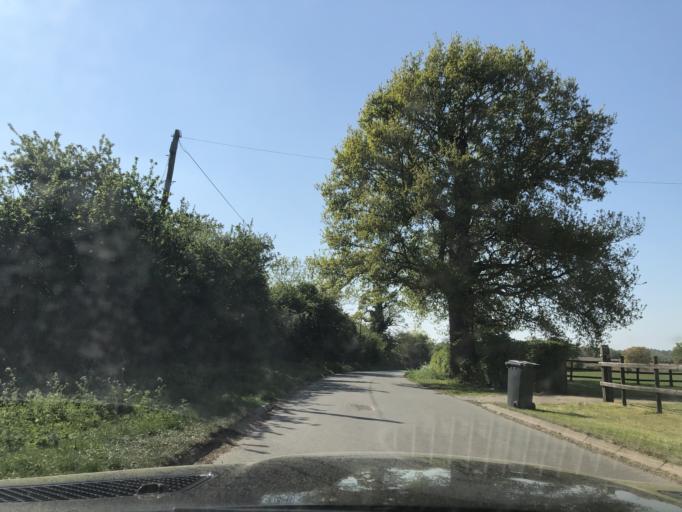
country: GB
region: England
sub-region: Warwickshire
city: Warwick
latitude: 52.2892
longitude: -1.6252
